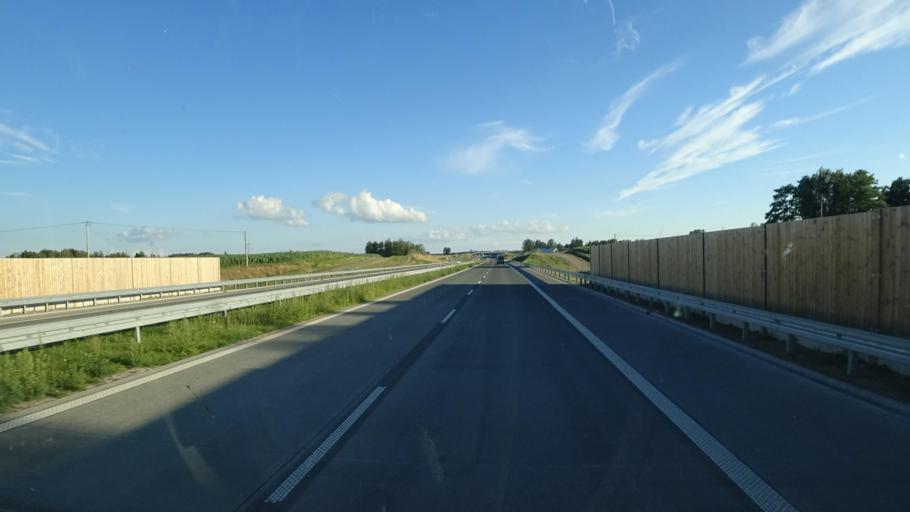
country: PL
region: Podlasie
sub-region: Powiat suwalski
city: Raczki
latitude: 53.9515
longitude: 22.7673
